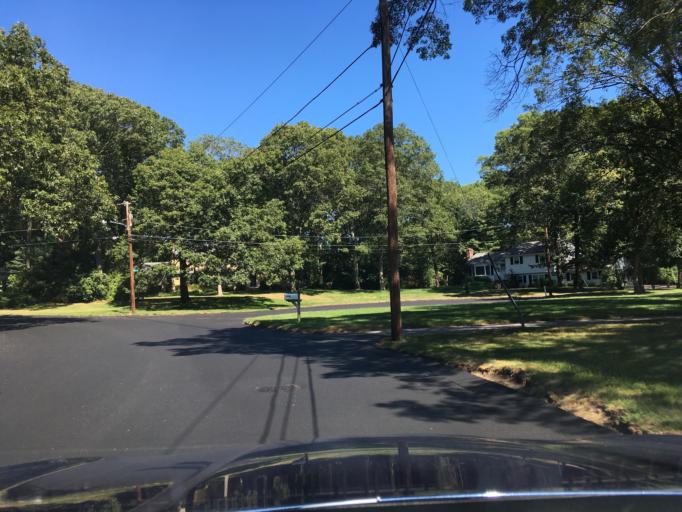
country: US
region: Rhode Island
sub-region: Kent County
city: East Greenwich
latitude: 41.6374
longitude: -71.4711
